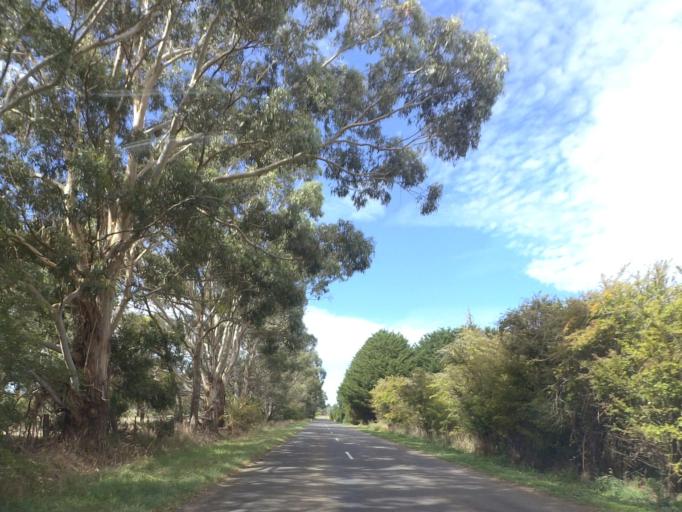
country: AU
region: Victoria
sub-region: Hume
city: Sunbury
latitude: -37.3227
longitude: 144.5373
